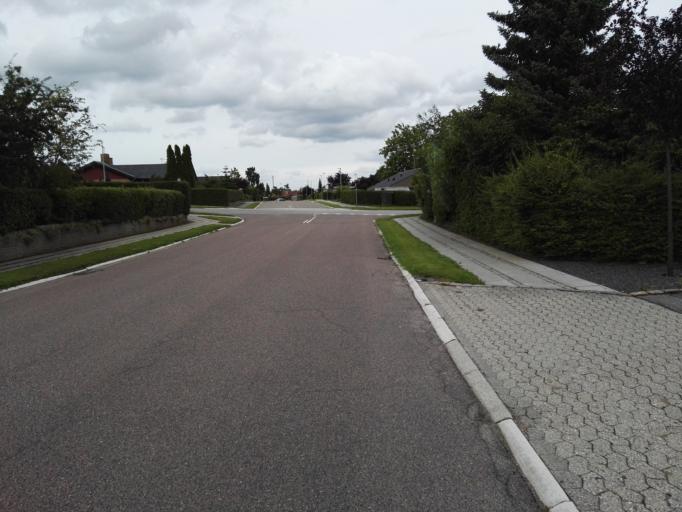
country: DK
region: Capital Region
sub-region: Egedal Kommune
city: Stenlose
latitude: 55.7683
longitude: 12.1839
